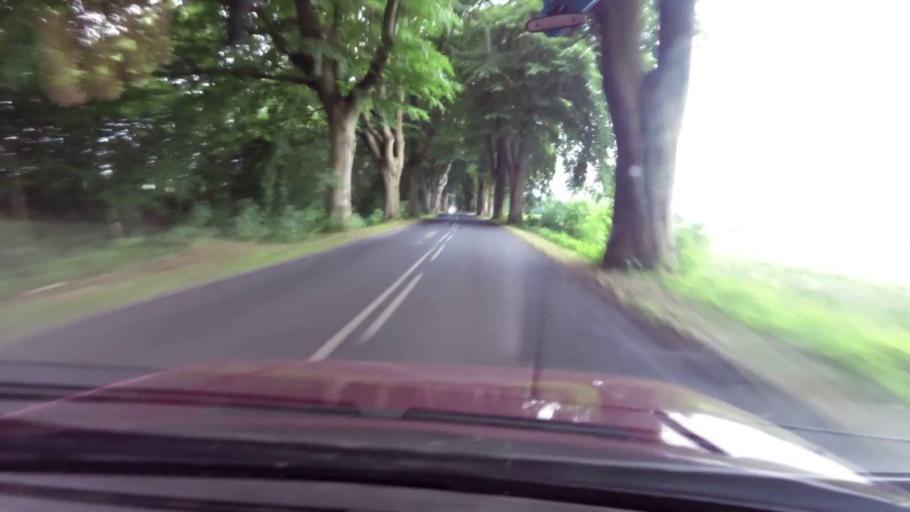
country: PL
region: West Pomeranian Voivodeship
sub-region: Powiat koszalinski
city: Polanow
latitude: 54.1419
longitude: 16.5383
